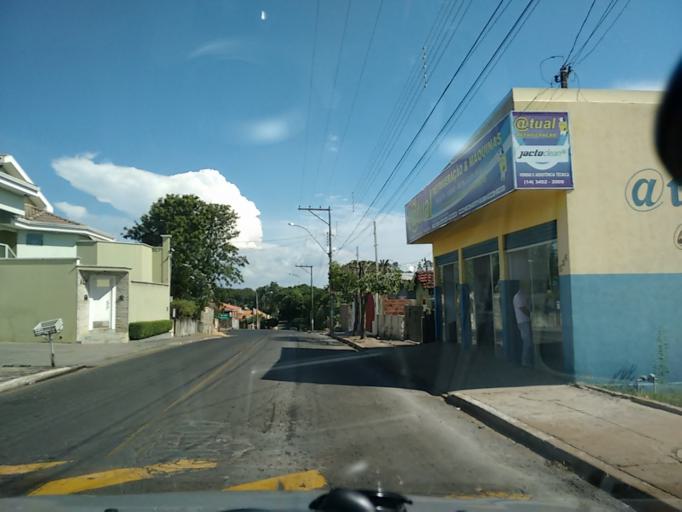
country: BR
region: Sao Paulo
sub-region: Pompeia
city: Pompeia
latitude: -22.1088
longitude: -50.1788
